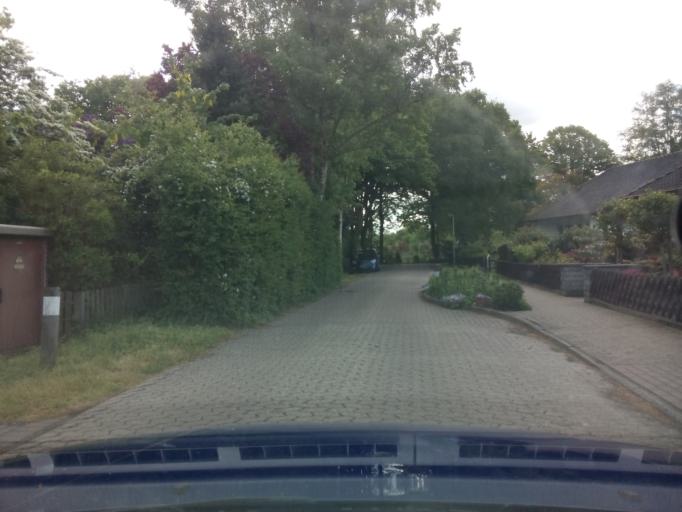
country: DE
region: Lower Saxony
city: Lilienthal
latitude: 53.1343
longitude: 8.9125
